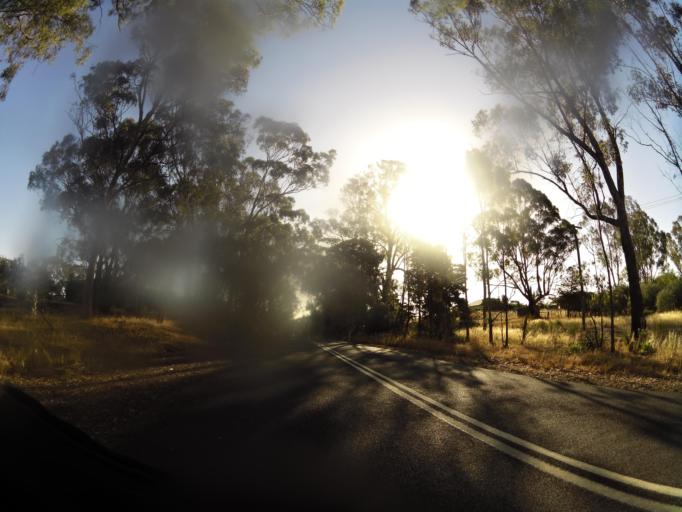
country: AU
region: Victoria
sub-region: Murrindindi
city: Kinglake West
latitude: -37.0211
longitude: 145.1058
